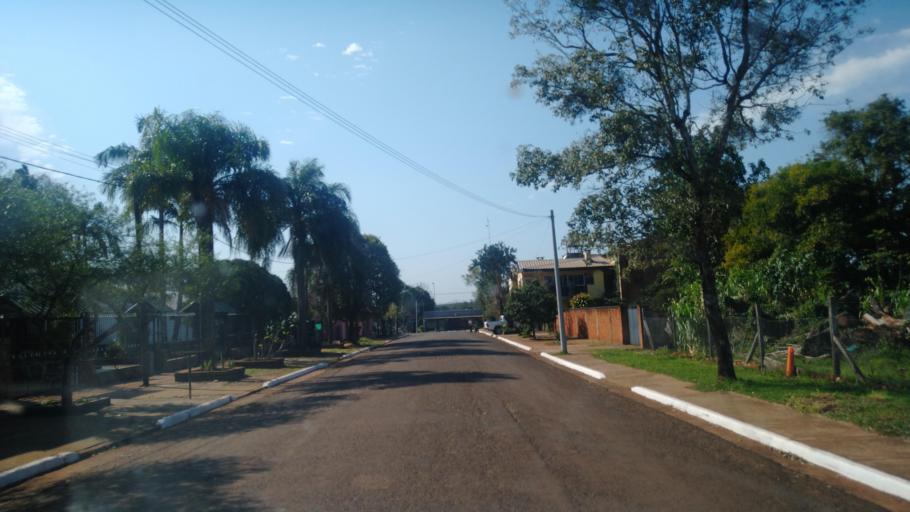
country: AR
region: Misiones
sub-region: Departamento de San Ignacio
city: San Ignacio
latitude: -27.2561
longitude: -55.5387
